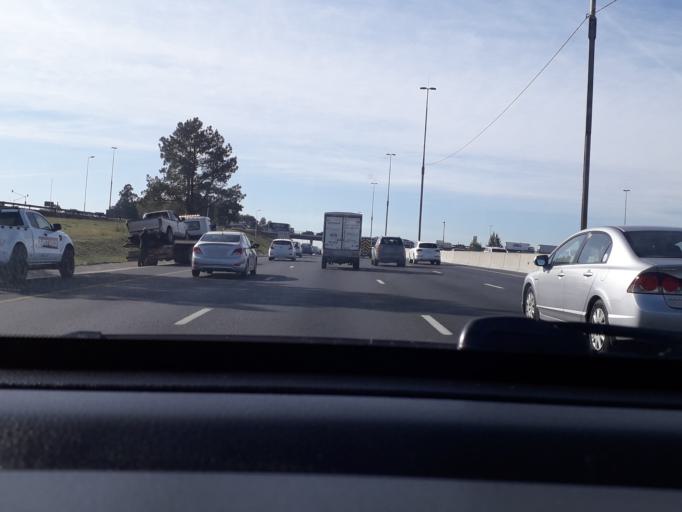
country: ZA
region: Gauteng
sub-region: City of Johannesburg Metropolitan Municipality
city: Modderfontein
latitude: -26.1025
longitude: 28.1233
